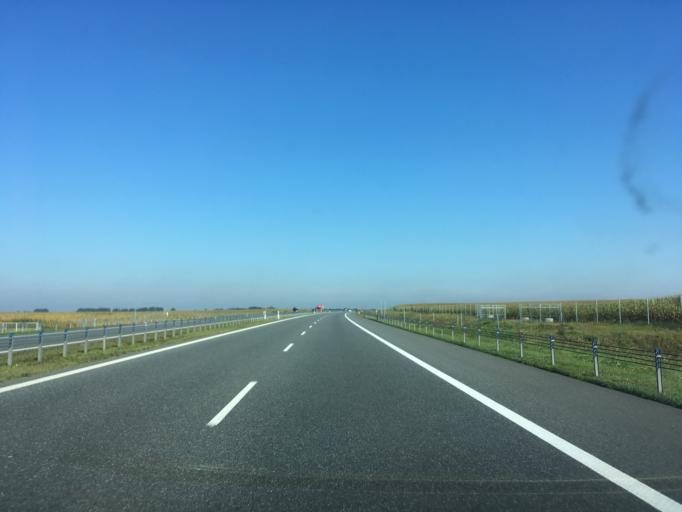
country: PL
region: Kujawsko-Pomorskie
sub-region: Powiat wabrzeski
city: Pluznica
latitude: 53.1808
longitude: 18.7375
